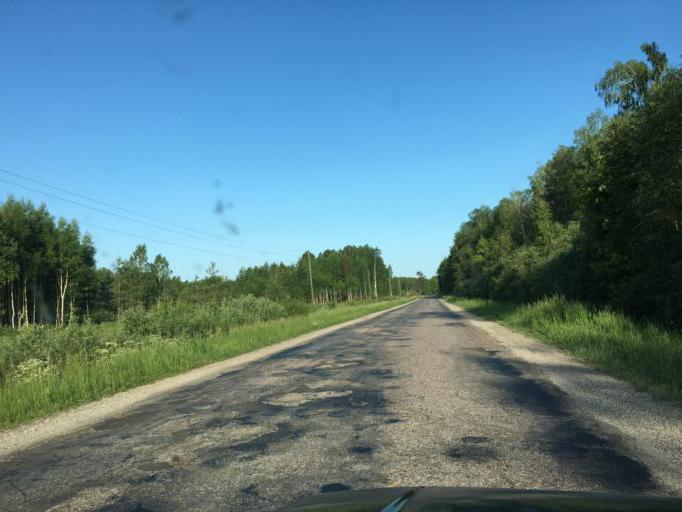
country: LV
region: Jelgava
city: Jelgava
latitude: 56.6550
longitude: 23.6092
